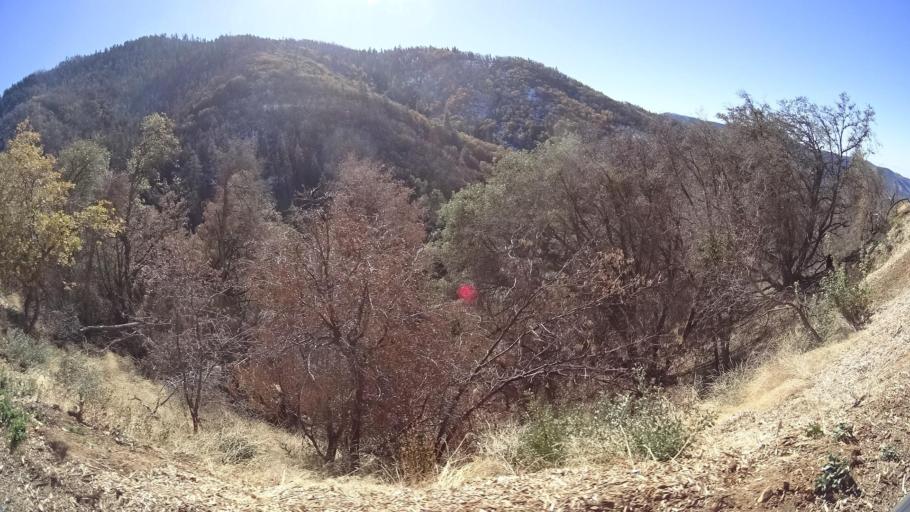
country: US
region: California
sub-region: Kern County
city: Alta Sierra
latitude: 35.7426
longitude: -118.5740
